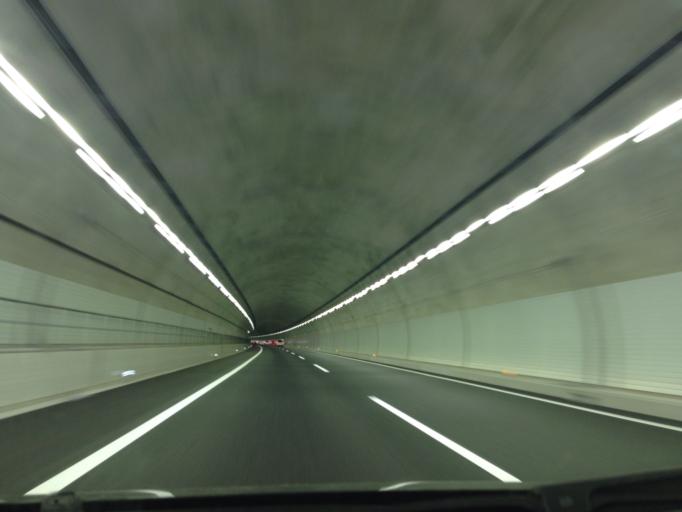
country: JP
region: Aichi
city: Okazaki
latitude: 34.9691
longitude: 137.2499
